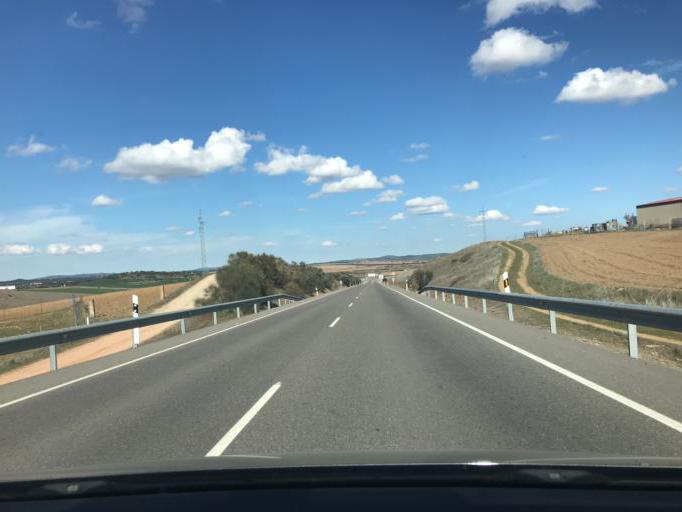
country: ES
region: Andalusia
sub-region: Province of Cordoba
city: Fuente Obejuna
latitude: 38.2711
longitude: -5.4308
